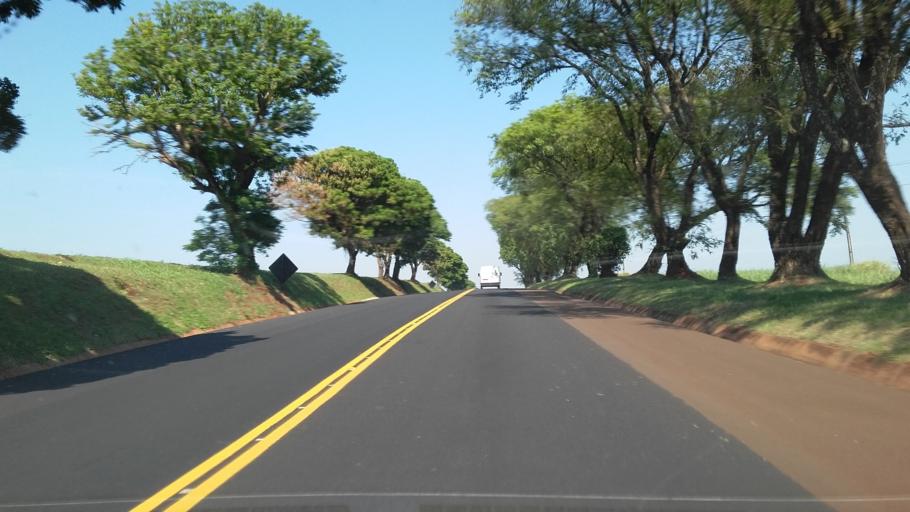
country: BR
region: Parana
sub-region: Bandeirantes
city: Bandeirantes
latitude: -23.1315
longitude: -50.4369
